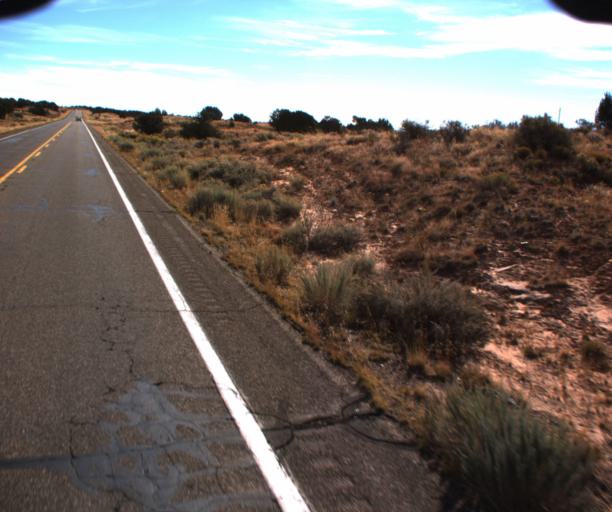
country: US
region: Arizona
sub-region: Coconino County
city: Kaibito
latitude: 36.5792
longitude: -111.1357
